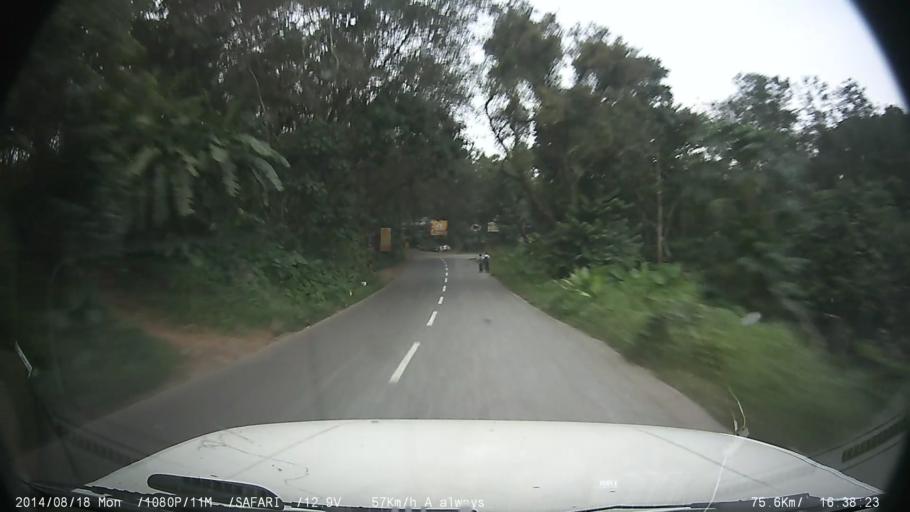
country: IN
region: Kerala
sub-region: Ernakulam
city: Piravam
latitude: 9.8263
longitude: 76.5840
